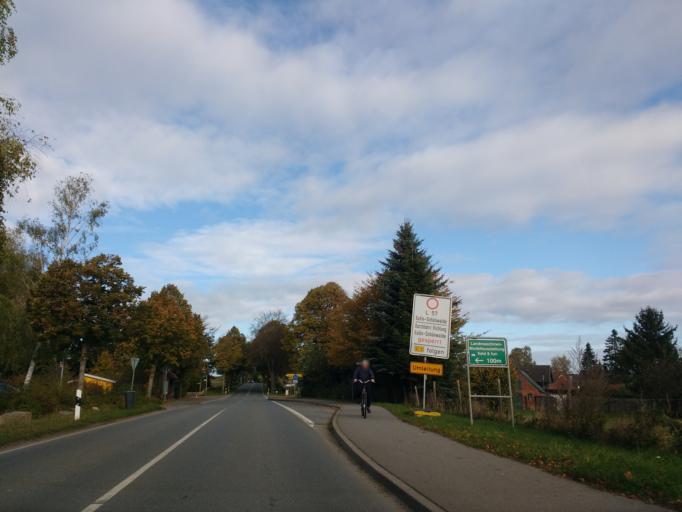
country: DE
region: Schleswig-Holstein
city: Altenkrempe
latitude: 54.1393
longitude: 10.8236
